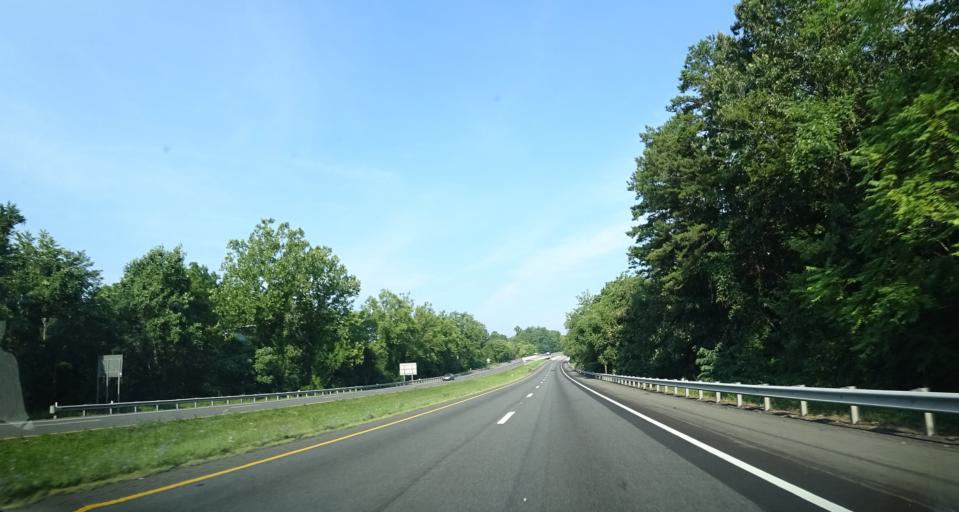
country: US
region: Virginia
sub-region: Fauquier County
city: Marshall
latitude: 38.9024
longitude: -77.9350
